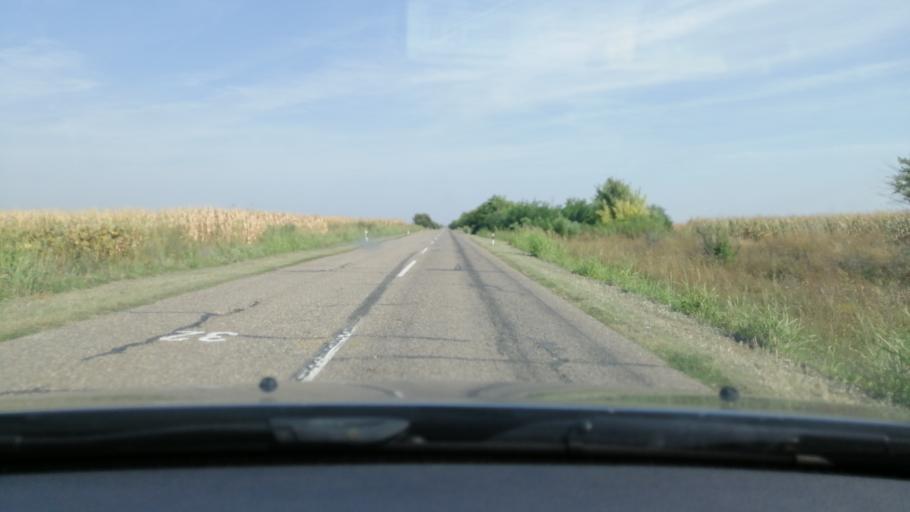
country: RS
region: Autonomna Pokrajina Vojvodina
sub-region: Juznobanatski Okrug
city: Kovacica
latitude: 45.1369
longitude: 20.6163
